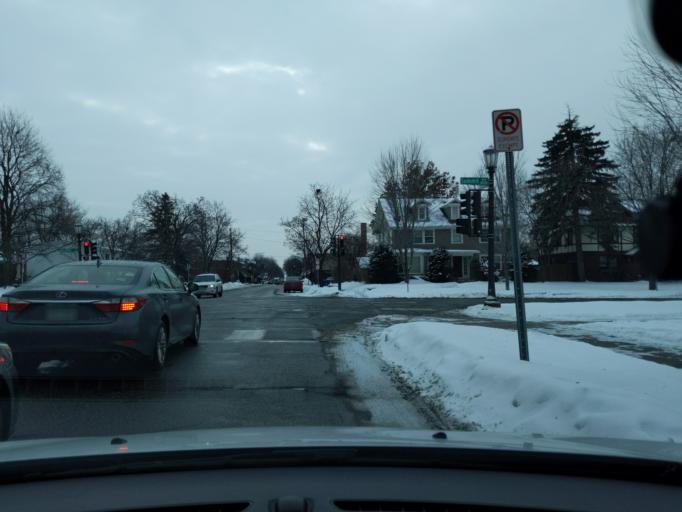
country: US
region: Minnesota
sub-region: Dakota County
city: West Saint Paul
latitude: 44.9416
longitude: -93.1365
